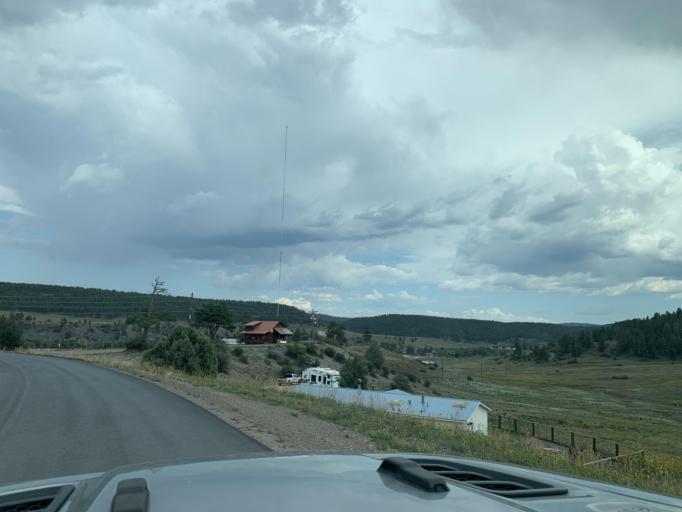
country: US
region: Colorado
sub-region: Archuleta County
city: Pagosa Springs
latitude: 37.2579
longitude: -107.0209
